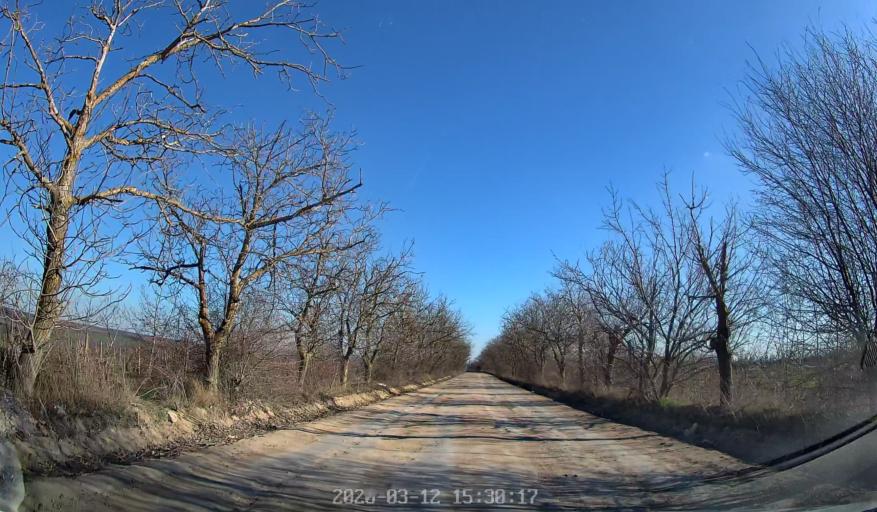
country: MD
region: Chisinau
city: Ciorescu
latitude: 47.1615
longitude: 28.9383
